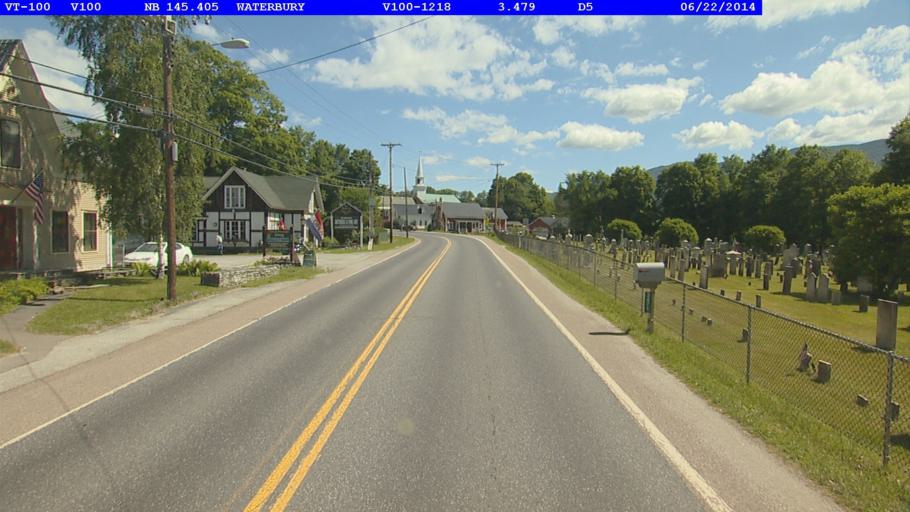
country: US
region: Vermont
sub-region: Washington County
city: Waterbury
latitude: 44.3795
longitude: -72.7215
